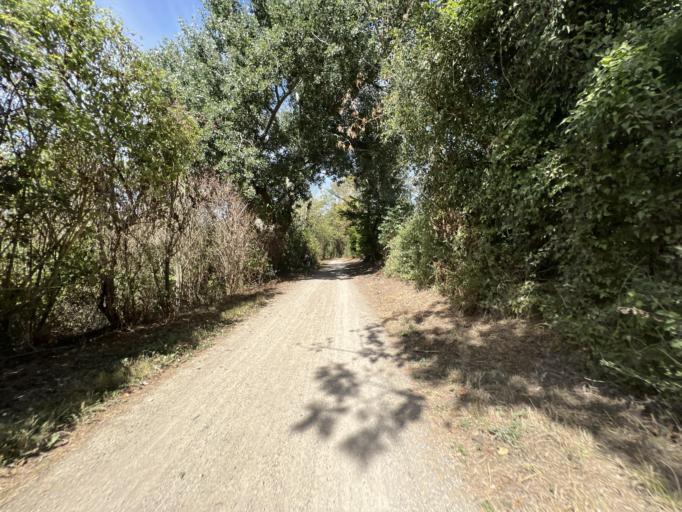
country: DE
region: North Rhine-Westphalia
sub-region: Regierungsbezirk Koln
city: Niederzier
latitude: 50.8458
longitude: 6.4403
